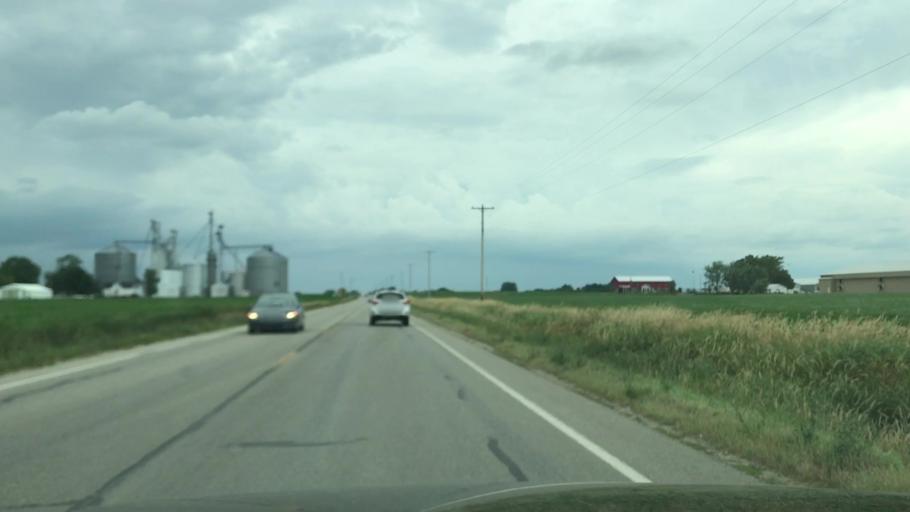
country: US
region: Michigan
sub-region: Ottawa County
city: Hudsonville
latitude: 42.8113
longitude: -85.8569
